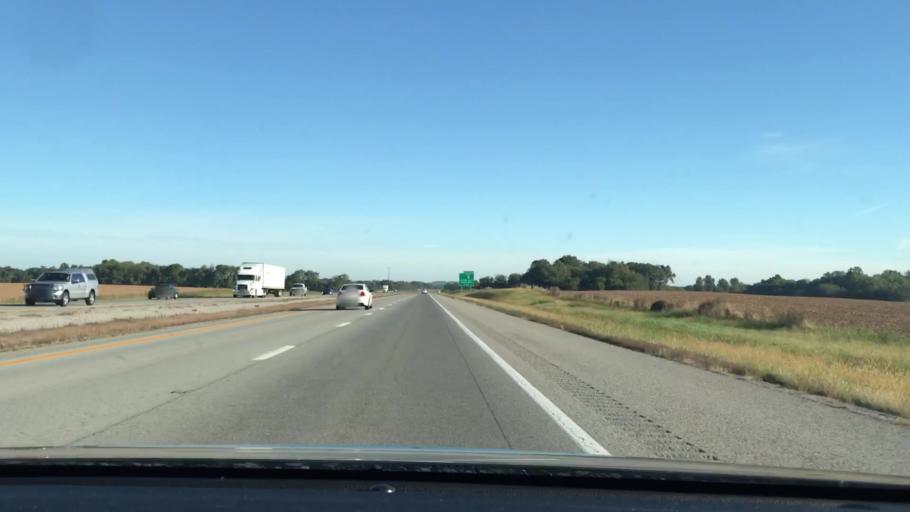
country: US
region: Kentucky
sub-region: Christian County
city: Hopkinsville
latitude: 36.7880
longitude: -87.4957
